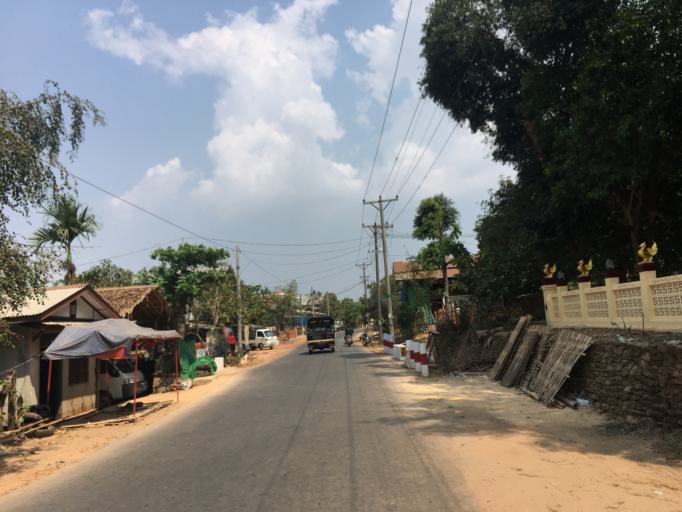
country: MM
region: Mon
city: Mawlamyine
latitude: 16.4679
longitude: 97.5217
